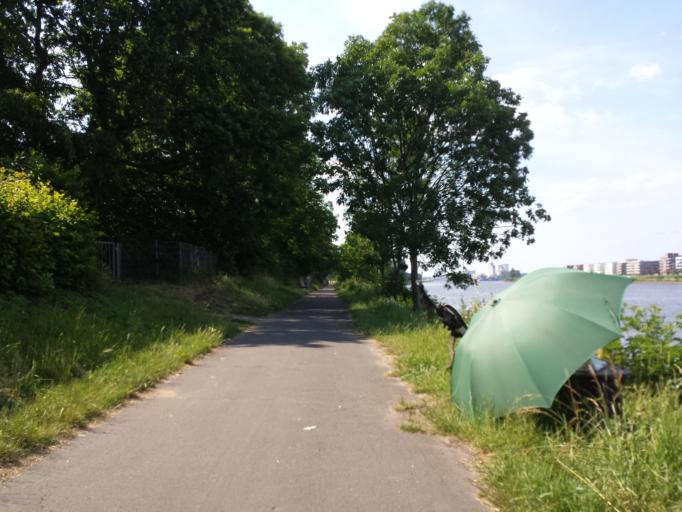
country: DE
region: Bremen
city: Bremen
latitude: 53.0942
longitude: 8.7587
